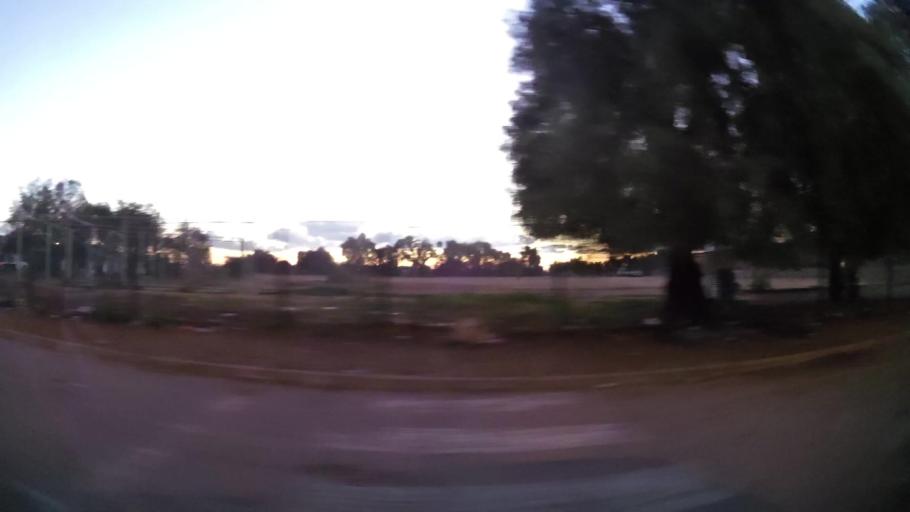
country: ZA
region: Northern Cape
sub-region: Frances Baard District Municipality
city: Kimberley
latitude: -28.7113
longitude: 24.7542
